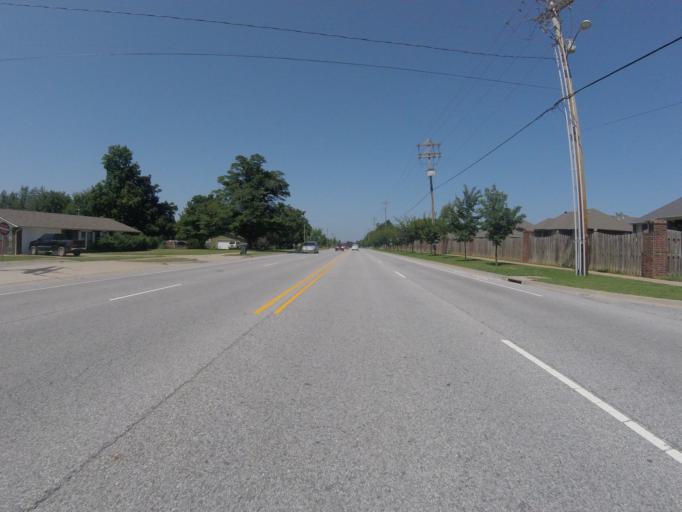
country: US
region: Arkansas
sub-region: Washington County
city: Fayetteville
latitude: 36.0928
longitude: -94.2039
